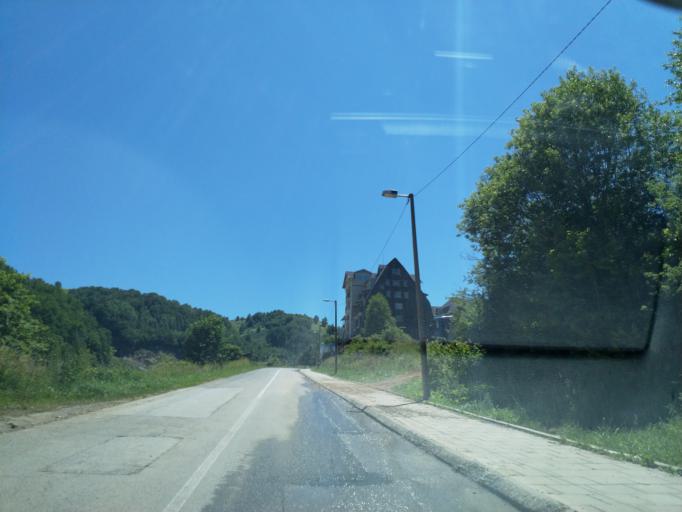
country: XK
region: Mitrovica
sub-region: Komuna e Leposaviqit
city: Leposaviq
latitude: 43.2896
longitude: 20.8801
